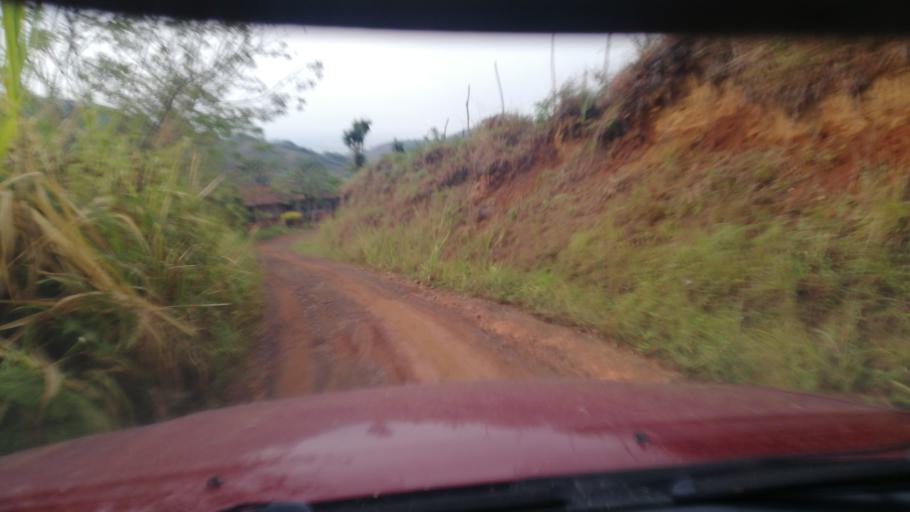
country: CO
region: Risaralda
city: Balboa
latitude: 4.8833
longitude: -75.9494
